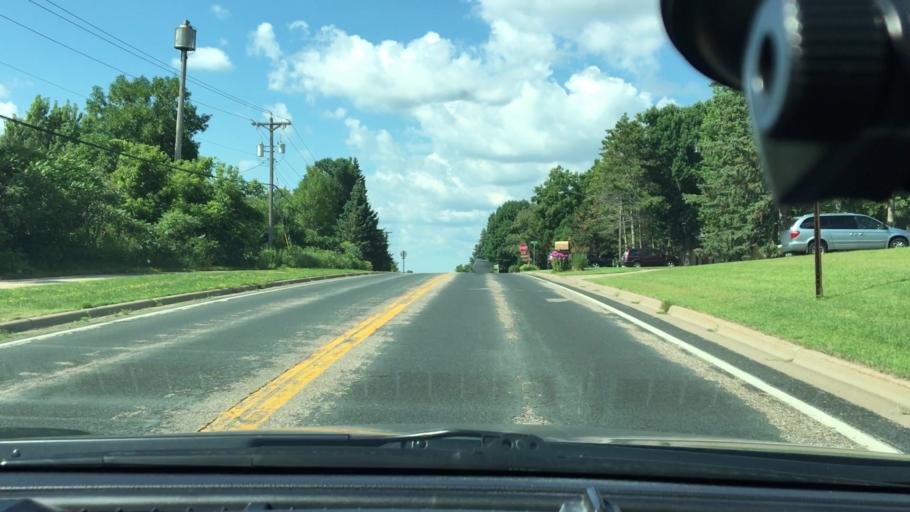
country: US
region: Minnesota
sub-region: Hennepin County
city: New Hope
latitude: 45.0428
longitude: -93.4210
